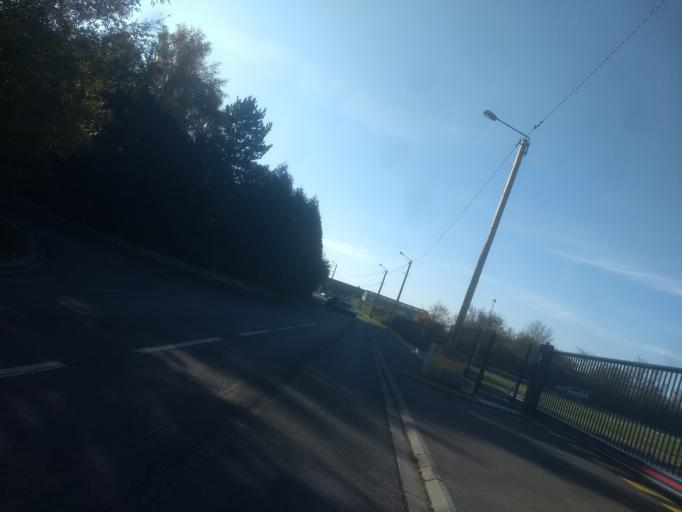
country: FR
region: Nord-Pas-de-Calais
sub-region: Departement du Pas-de-Calais
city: Achicourt
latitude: 50.2772
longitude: 2.7695
